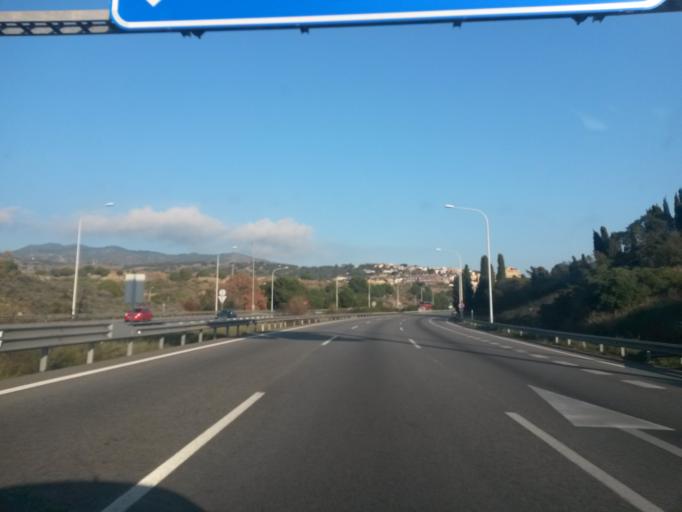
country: ES
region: Catalonia
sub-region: Provincia de Barcelona
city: Alella
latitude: 41.4885
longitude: 2.3001
